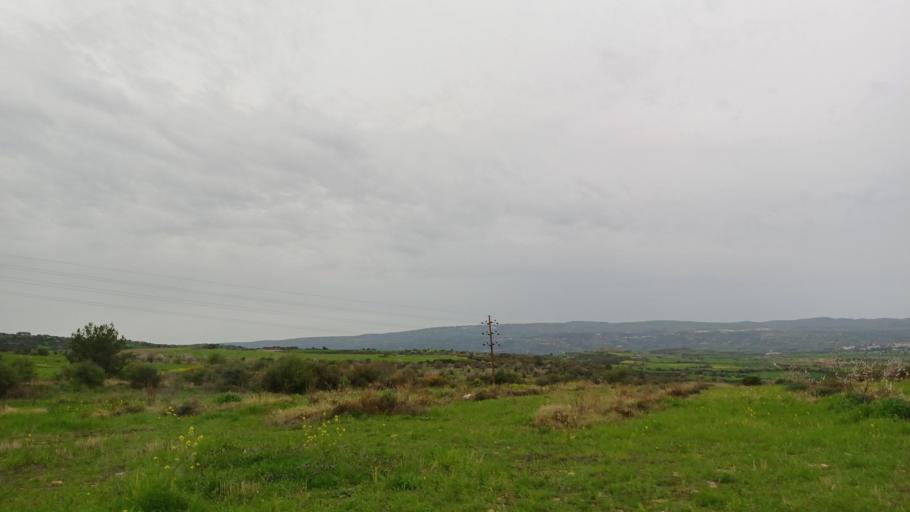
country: CY
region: Pafos
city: Polis
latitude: 35.0474
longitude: 32.4732
